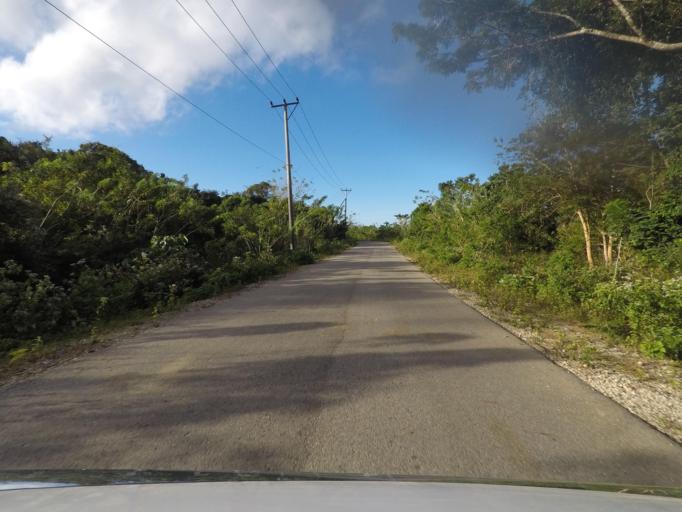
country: TL
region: Lautem
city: Lospalos
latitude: -8.4096
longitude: 126.9989
